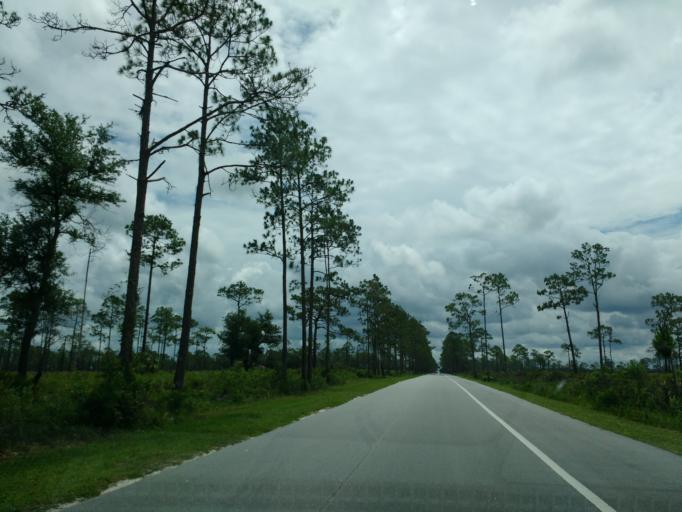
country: US
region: Florida
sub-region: Highlands County
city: Sebring
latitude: 27.4709
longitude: -81.5241
